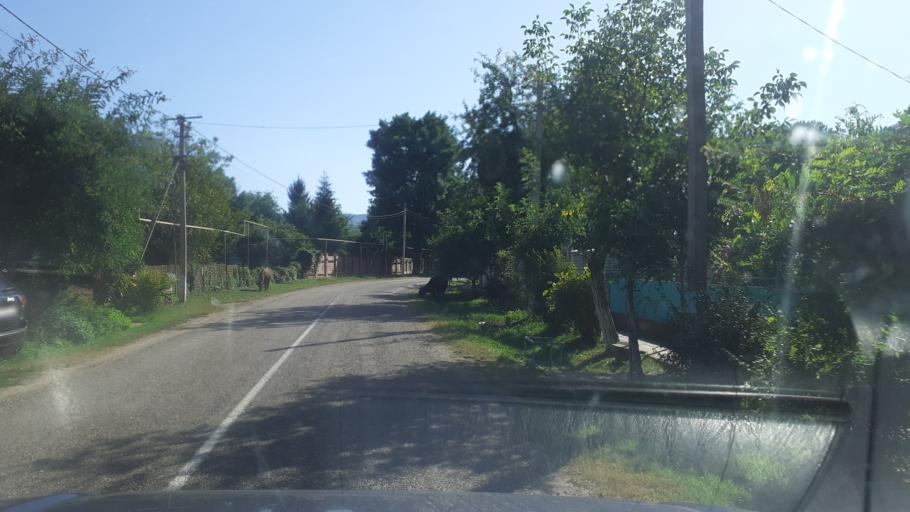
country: RU
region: Krasnodarskiy
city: Azovskaya
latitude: 44.7386
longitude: 38.5416
